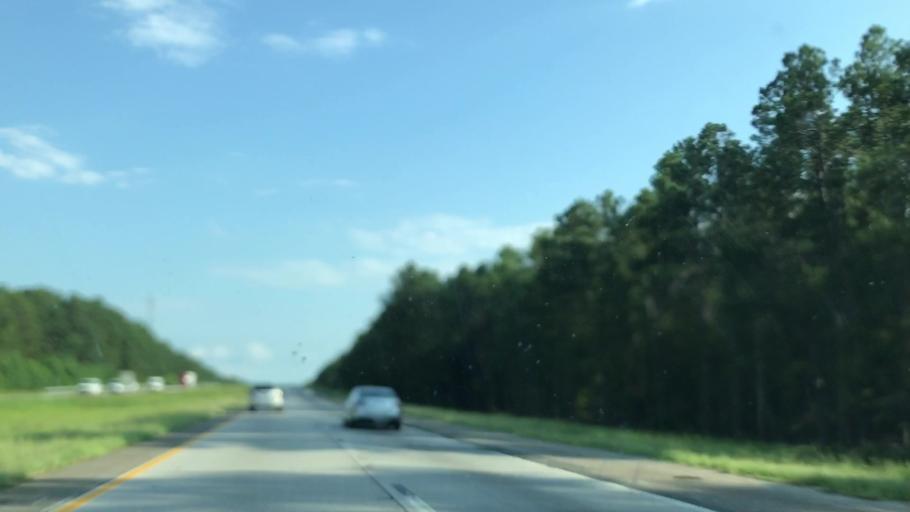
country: US
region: South Carolina
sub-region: Colleton County
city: Walterboro
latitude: 33.0399
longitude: -80.6694
